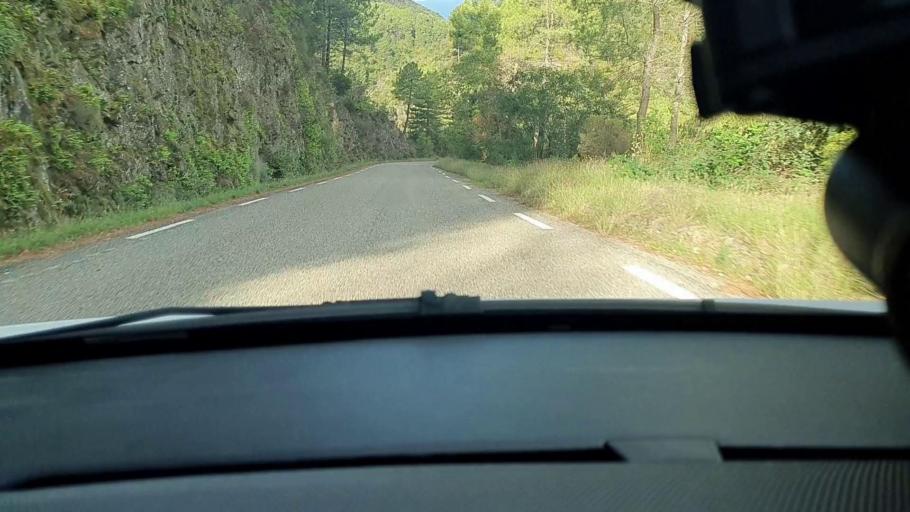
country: FR
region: Languedoc-Roussillon
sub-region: Departement du Gard
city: Besseges
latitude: 44.3175
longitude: 4.0401
